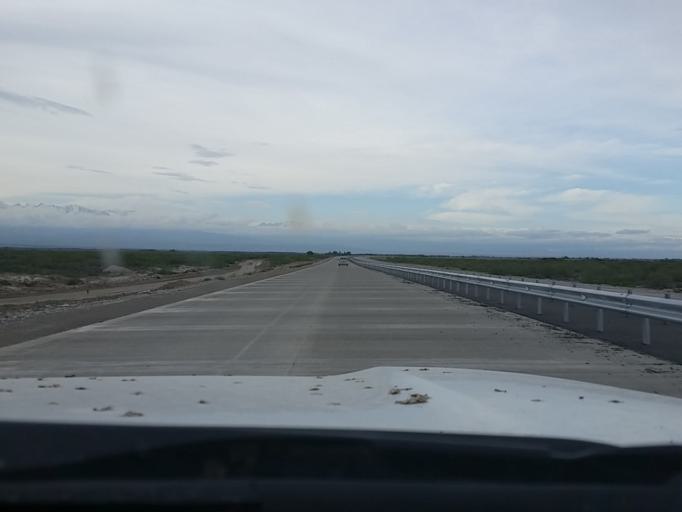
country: KZ
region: Almaty Oblysy
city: Zharkent
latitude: 44.0914
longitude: 80.0553
